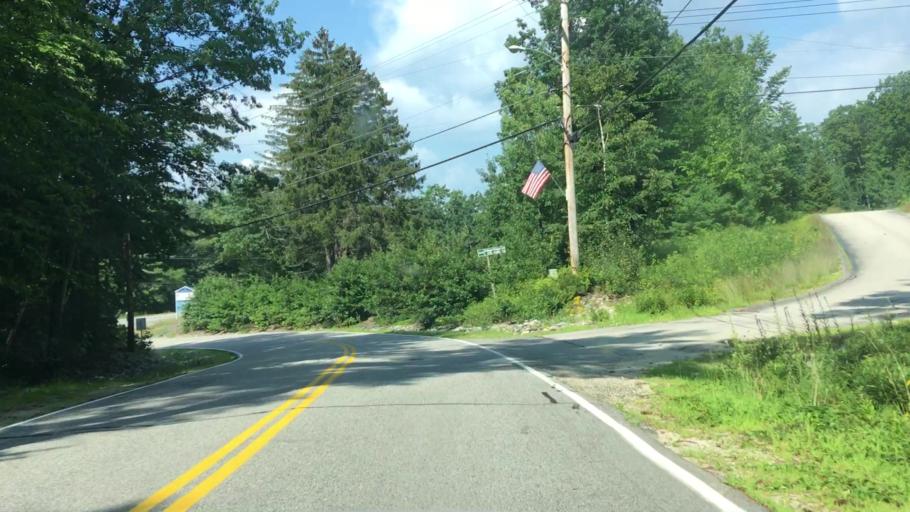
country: US
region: Maine
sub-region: Cumberland County
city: Raymond
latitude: 43.9026
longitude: -70.4785
